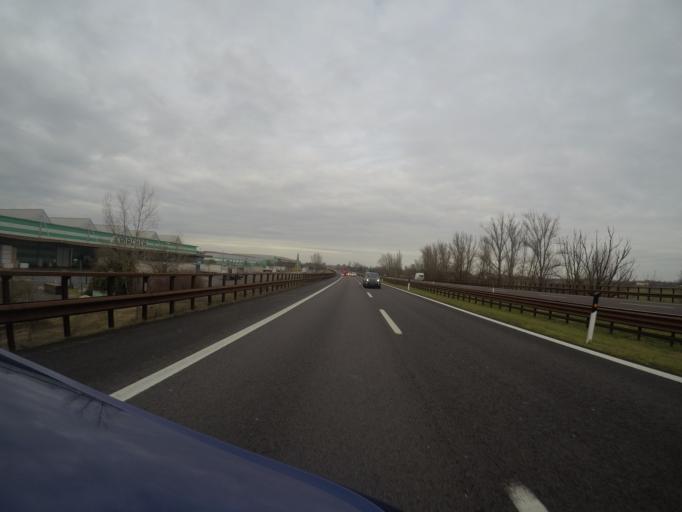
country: IT
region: Emilia-Romagna
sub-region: Provincia di Reggio Emilia
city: Rolo
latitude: 44.8920
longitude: 10.8504
